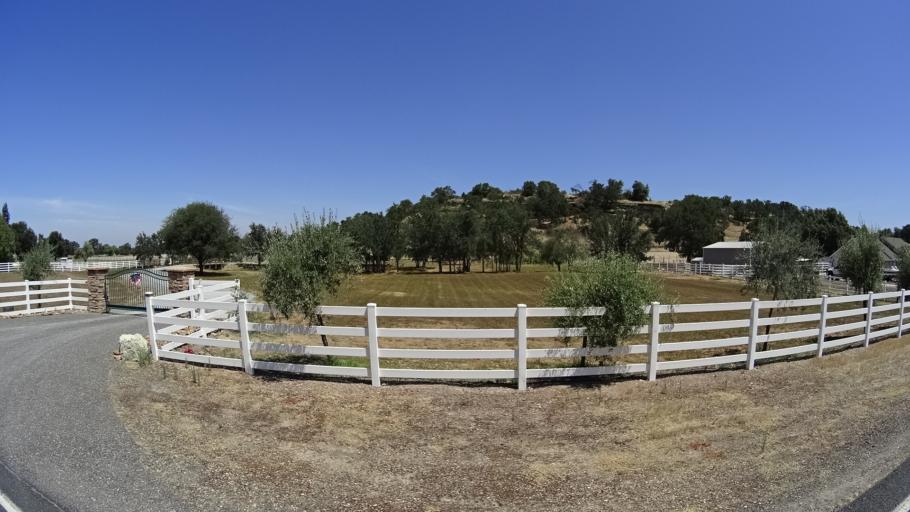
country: US
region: California
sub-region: Calaveras County
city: Rancho Calaveras
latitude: 38.1631
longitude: -120.9450
